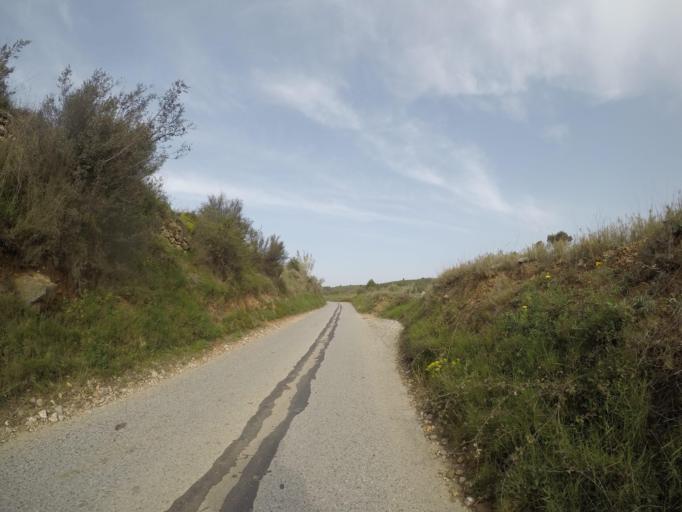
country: FR
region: Languedoc-Roussillon
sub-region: Departement des Pyrenees-Orientales
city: Baixas
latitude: 42.7678
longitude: 2.8106
